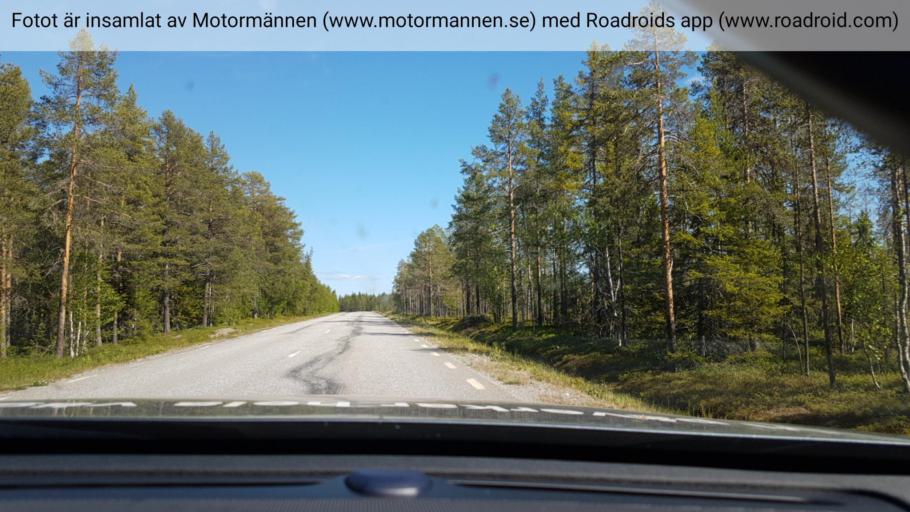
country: SE
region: Vaesterbotten
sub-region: Lycksele Kommun
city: Soderfors
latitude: 64.6239
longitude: 18.0993
